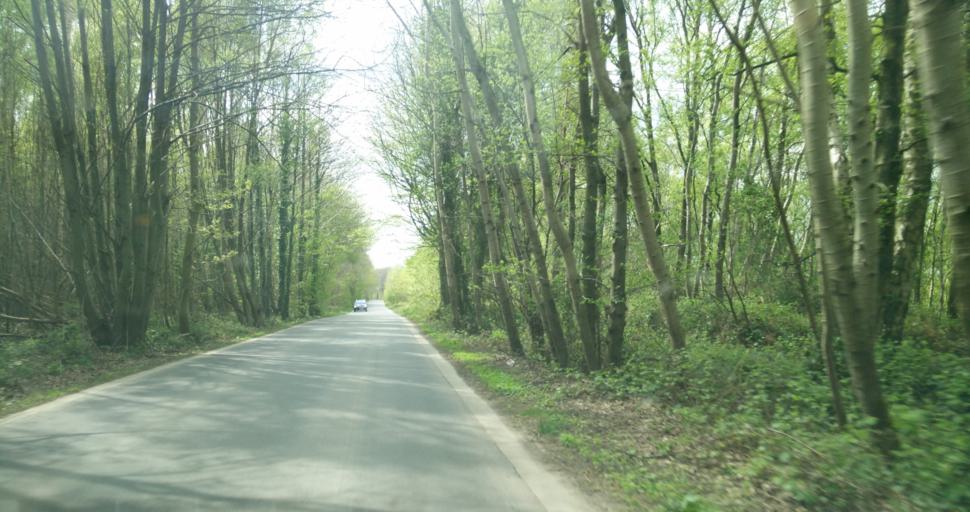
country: BE
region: Wallonia
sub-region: Province du Hainaut
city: Braine-le-Comte
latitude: 50.6297
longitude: 4.1915
